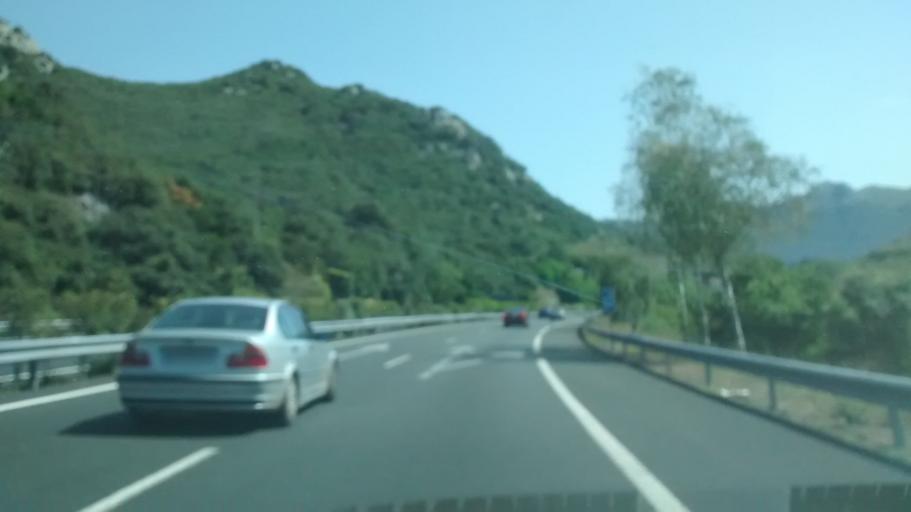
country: ES
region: Cantabria
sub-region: Provincia de Cantabria
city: Liendo
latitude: 43.3903
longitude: -3.3402
